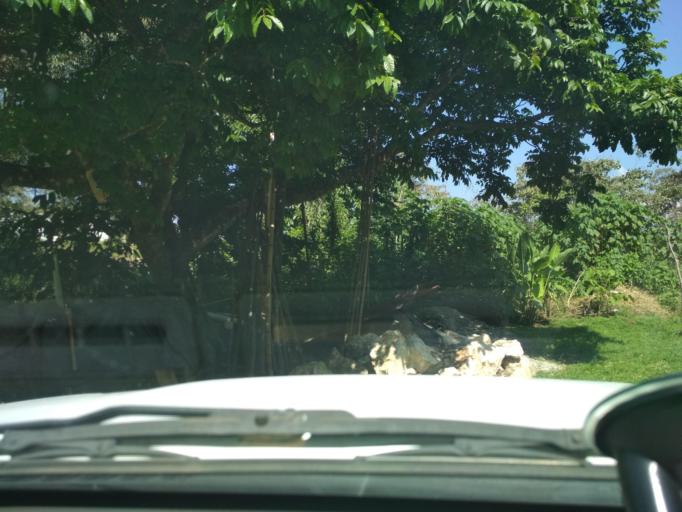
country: MX
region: Veracruz
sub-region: Fortin
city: Fraccionamiento Villas de la Llave
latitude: 18.9171
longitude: -96.9823
